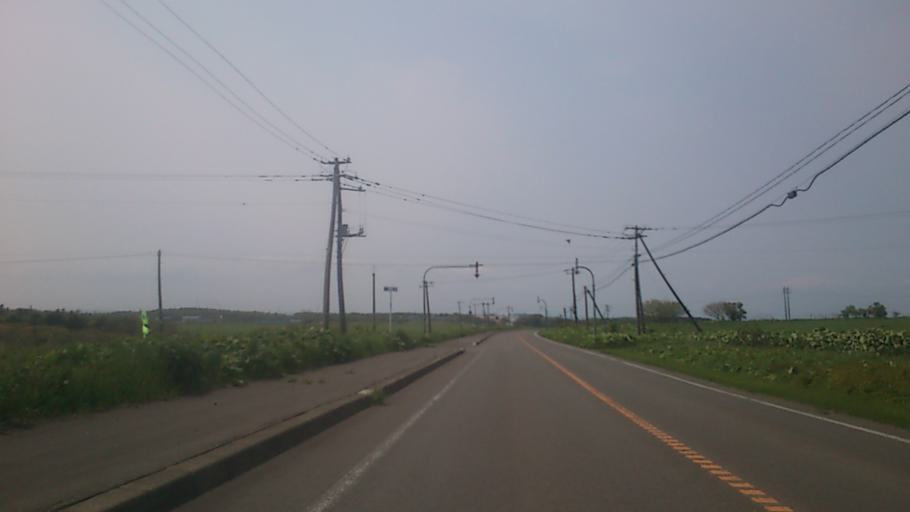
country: JP
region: Hokkaido
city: Nemuro
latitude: 43.2741
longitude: 145.5301
